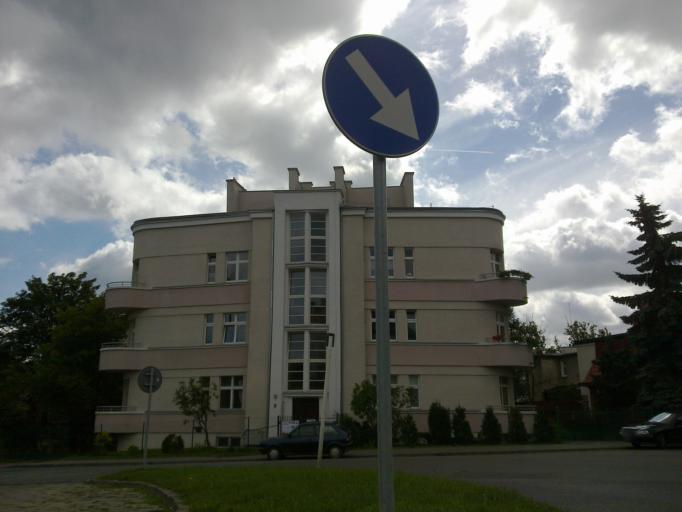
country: PL
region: Pomeranian Voivodeship
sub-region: Gdynia
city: Gdynia
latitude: 54.5125
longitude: 18.5458
